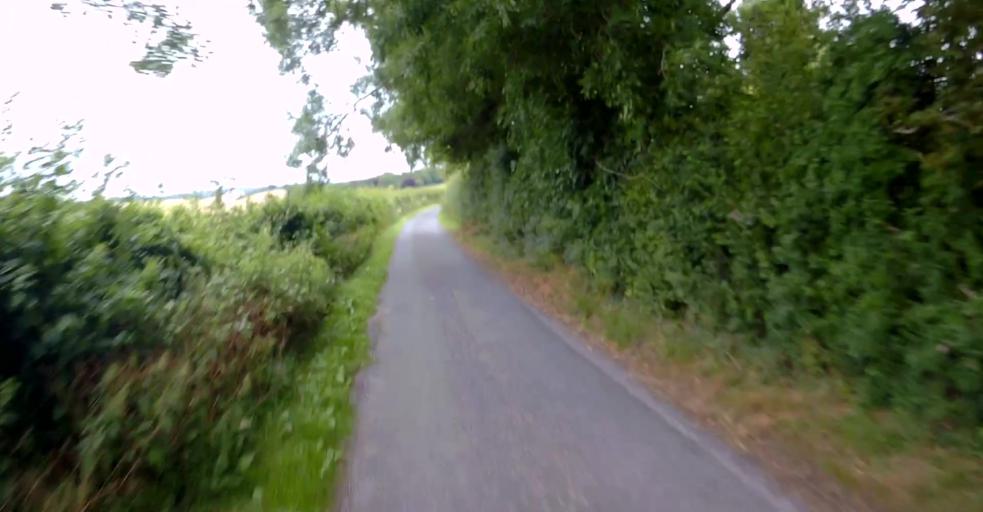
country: GB
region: England
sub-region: Hampshire
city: Kings Worthy
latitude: 51.0510
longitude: -1.2120
